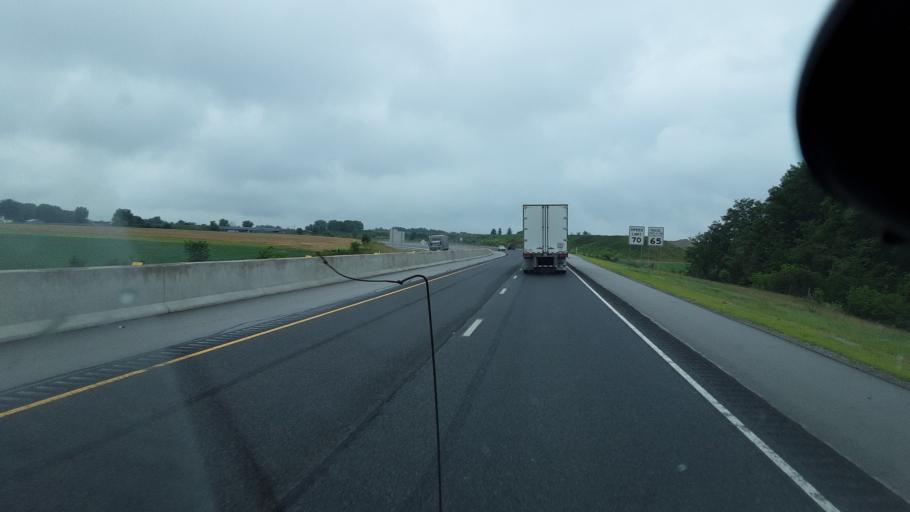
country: US
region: Indiana
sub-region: Allen County
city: New Haven
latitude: 40.9824
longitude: -85.0977
